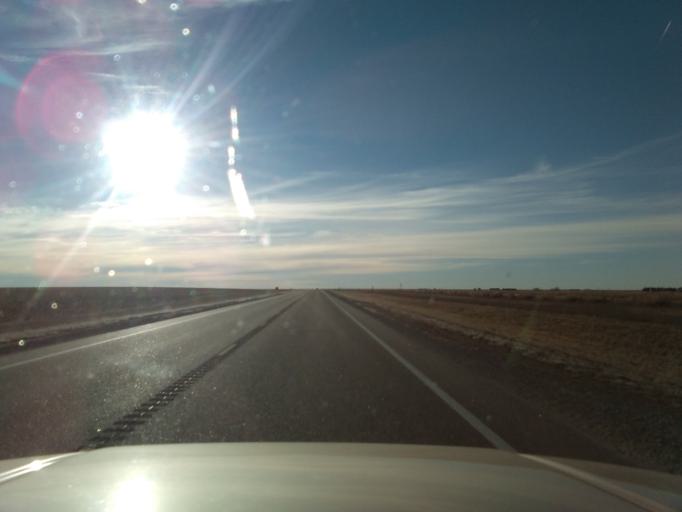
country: US
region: Kansas
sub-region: Sheridan County
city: Hoxie
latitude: 39.5163
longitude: -100.6321
